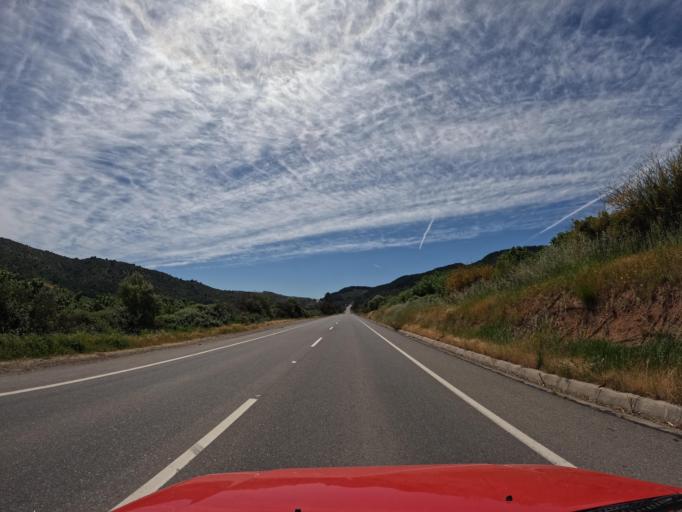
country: CL
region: Maule
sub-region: Provincia de Talca
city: Talca
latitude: -35.2551
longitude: -71.5429
